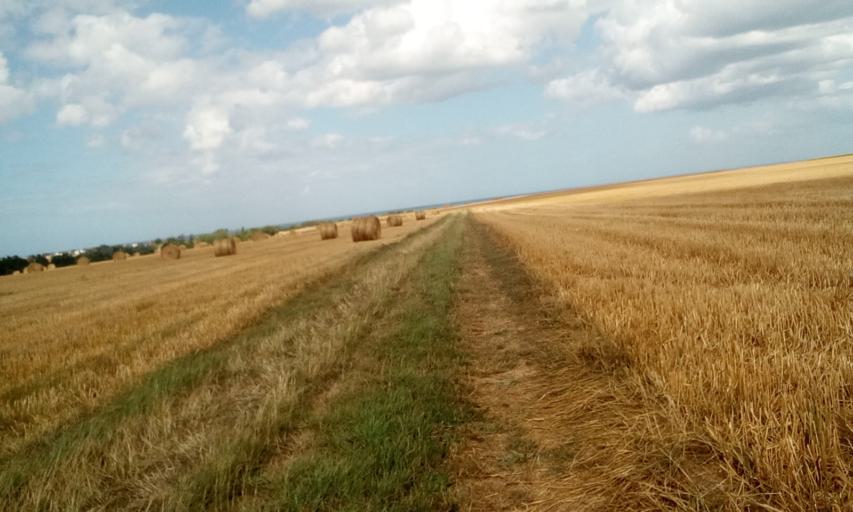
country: FR
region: Lower Normandy
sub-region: Departement du Calvados
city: Ver-sur-Mer
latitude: 49.3295
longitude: -0.5209
